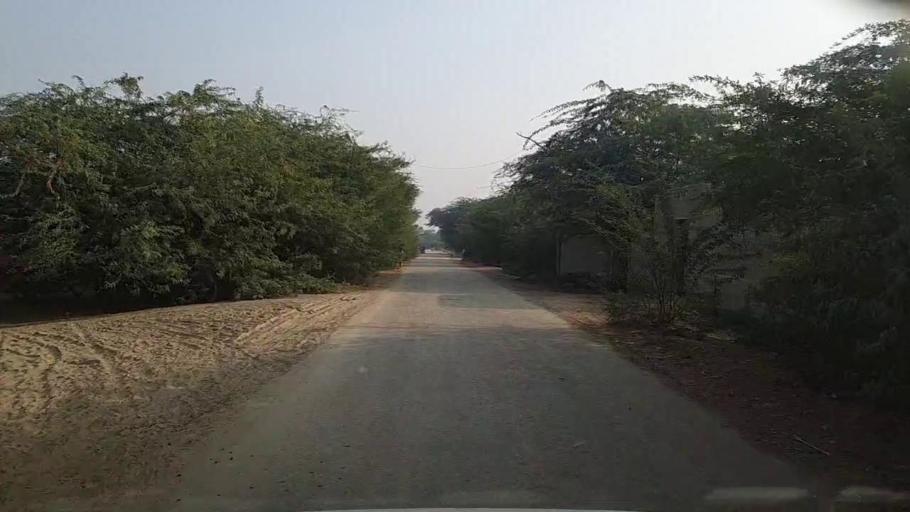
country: PK
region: Sindh
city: Kandiari
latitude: 27.0388
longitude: 68.4794
